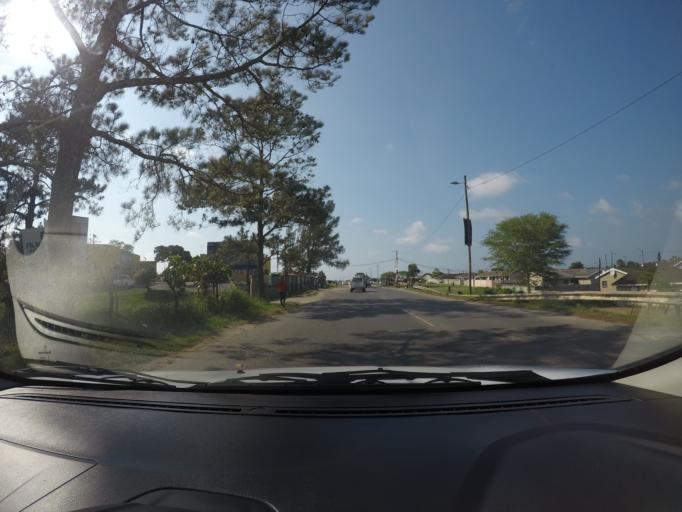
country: ZA
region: KwaZulu-Natal
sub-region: uThungulu District Municipality
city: eSikhawini
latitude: -28.8673
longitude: 31.9264
